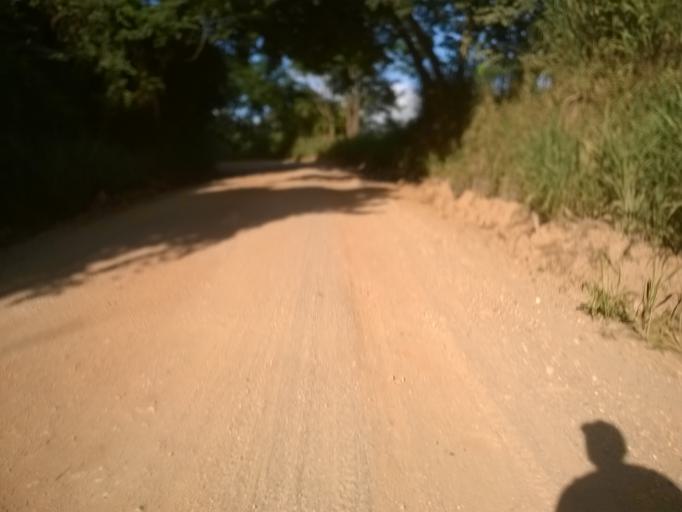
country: BR
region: Minas Gerais
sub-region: Uba
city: Uba
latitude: -21.0818
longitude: -42.9988
